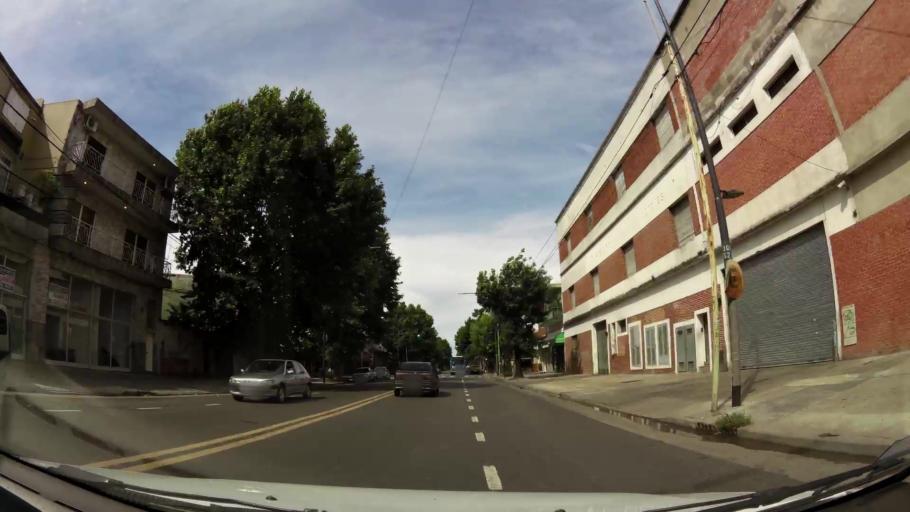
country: AR
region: Buenos Aires F.D.
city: Villa Lugano
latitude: -34.6492
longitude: -58.5095
